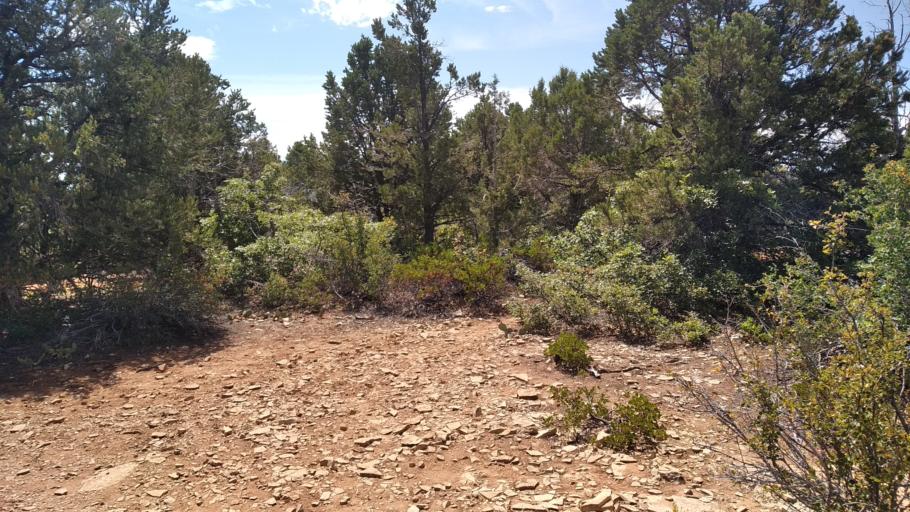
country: US
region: Utah
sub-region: Washington County
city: Hildale
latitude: 37.2896
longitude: -112.9288
